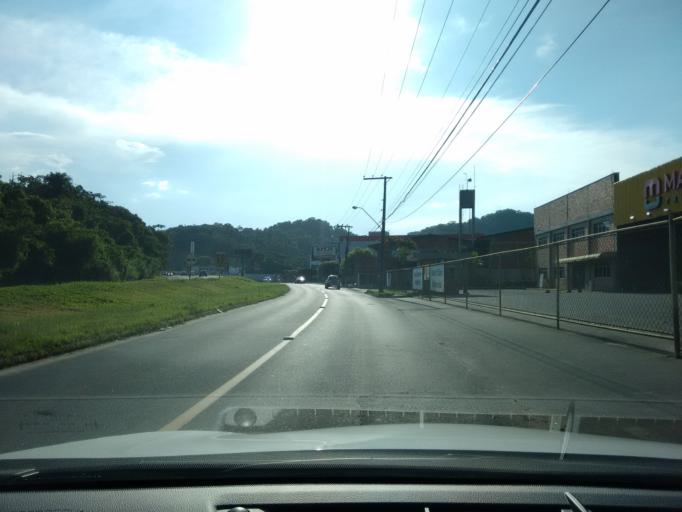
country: BR
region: Santa Catarina
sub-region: Blumenau
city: Blumenau
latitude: -26.8621
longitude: -49.0950
